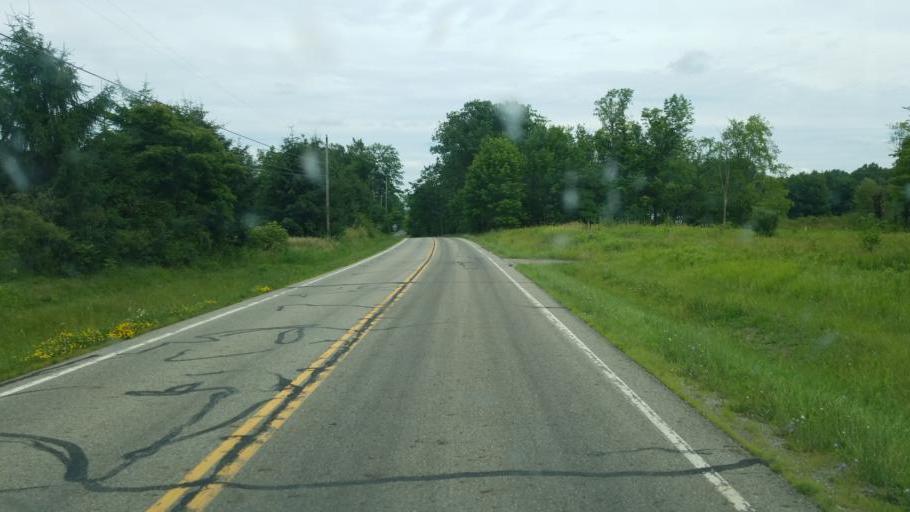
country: US
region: Ohio
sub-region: Geauga County
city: Bainbridge
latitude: 41.4217
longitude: -81.2475
